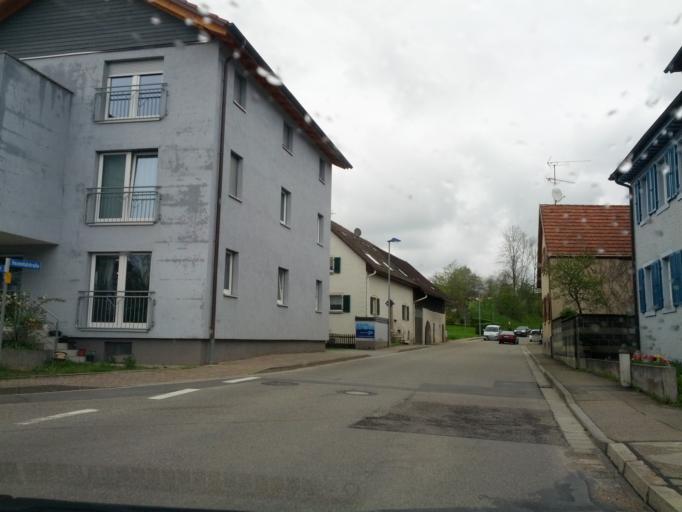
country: DE
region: Baden-Wuerttemberg
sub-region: Freiburg Region
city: Bollschweil
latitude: 47.9215
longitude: 7.7899
